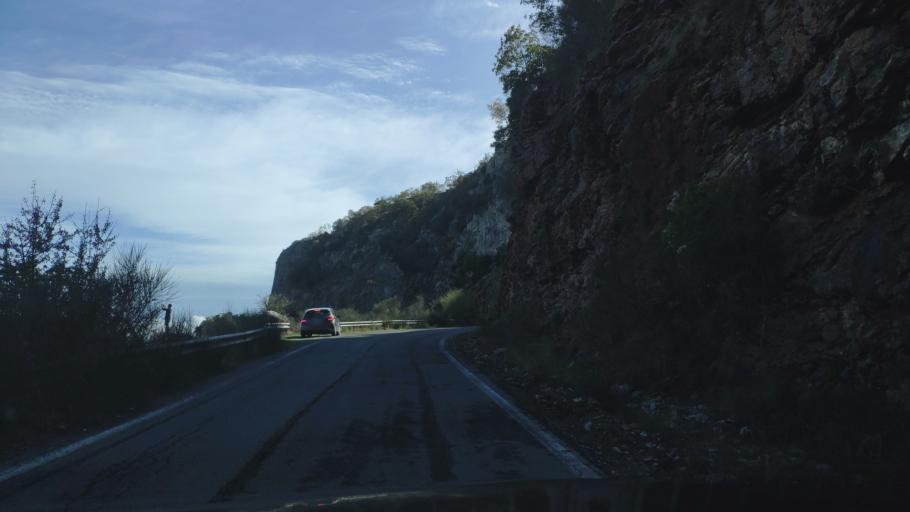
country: GR
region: Peloponnese
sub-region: Nomos Arkadias
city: Dimitsana
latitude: 37.5950
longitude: 22.0306
